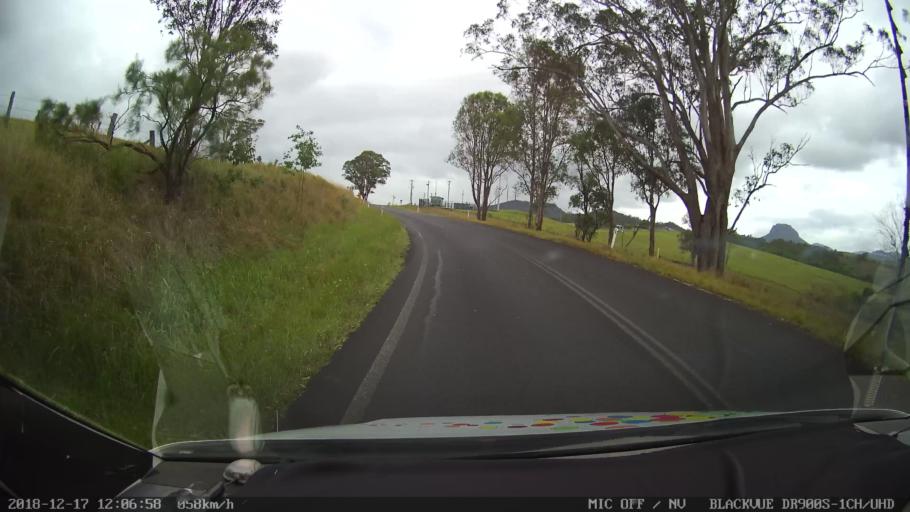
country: AU
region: New South Wales
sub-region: Kyogle
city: Kyogle
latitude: -28.4770
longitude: 152.5663
